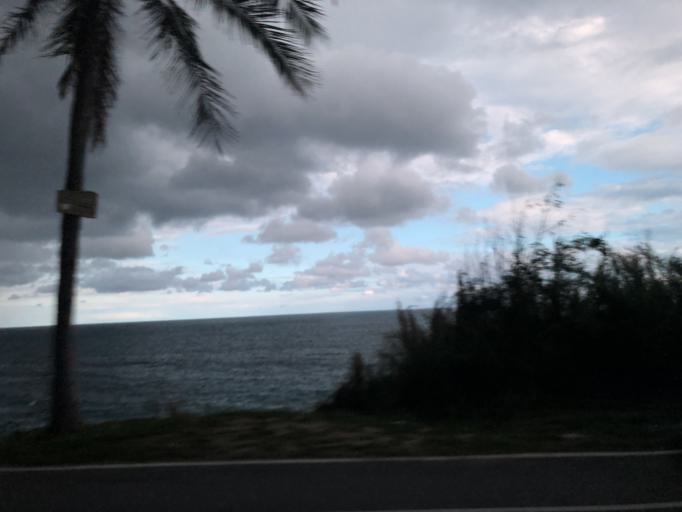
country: TW
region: Taiwan
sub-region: Taitung
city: Taitung
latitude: 22.8584
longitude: 121.1987
